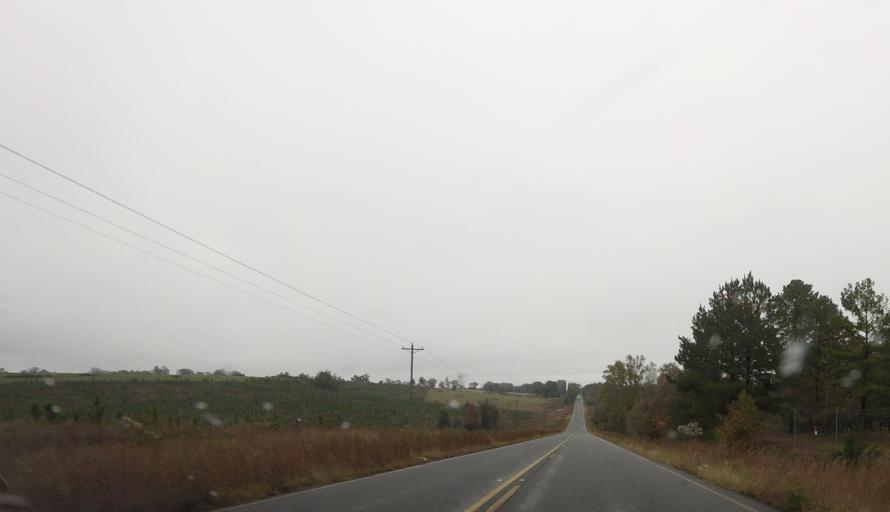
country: US
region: Georgia
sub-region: Marion County
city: Buena Vista
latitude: 32.4145
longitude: -84.3979
